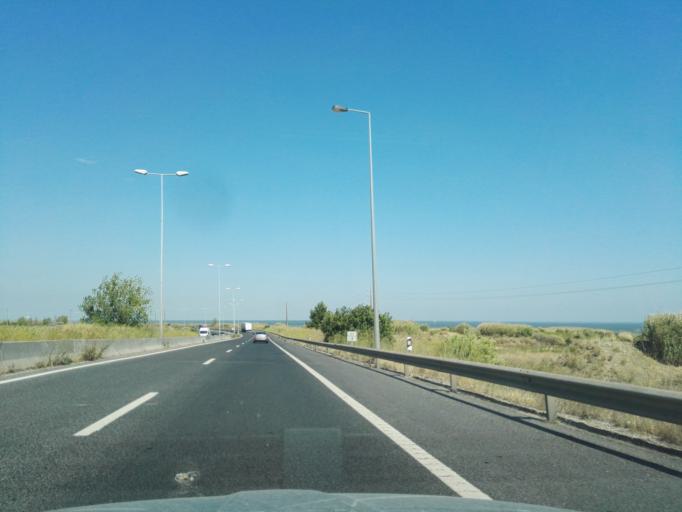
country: PT
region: Lisbon
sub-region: Loures
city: Bobadela
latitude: 38.7986
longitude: -9.0961
